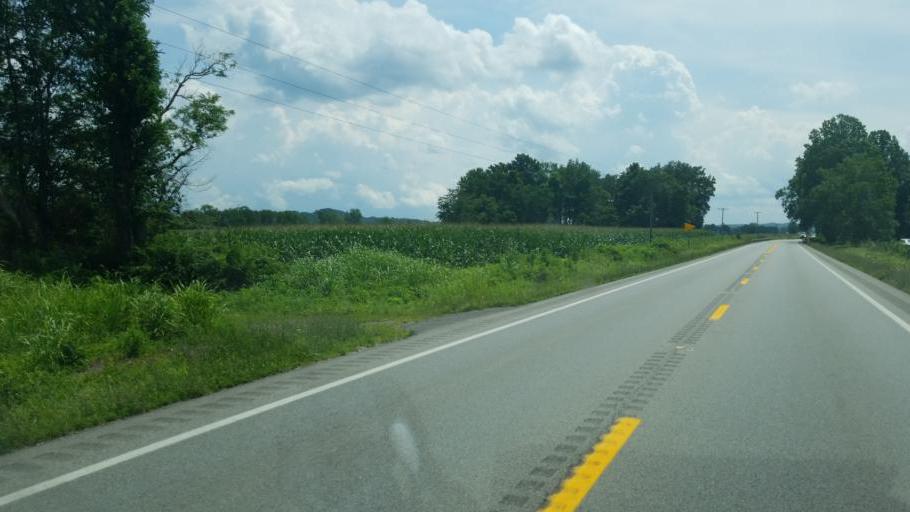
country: US
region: West Virginia
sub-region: Putnam County
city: Buffalo
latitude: 38.6863
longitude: -81.9648
